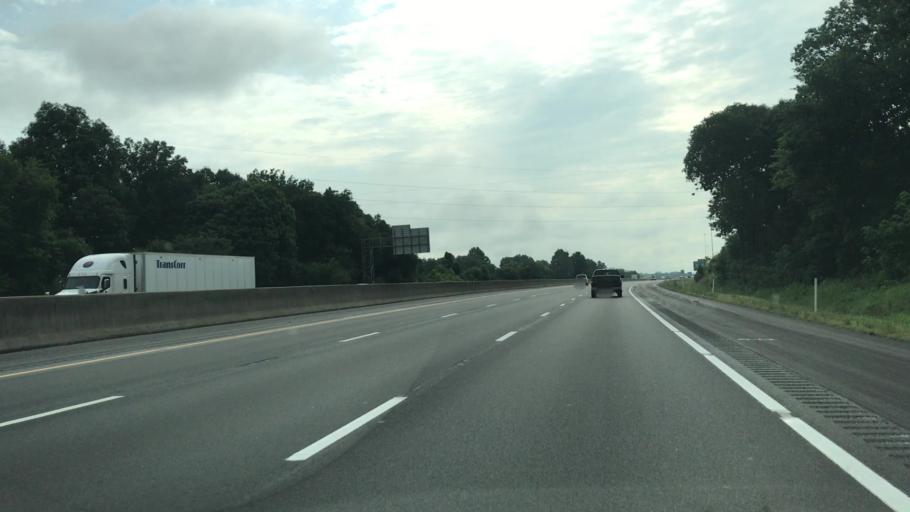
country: US
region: Kentucky
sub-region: Warren County
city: Bowling Green
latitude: 37.0098
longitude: -86.3508
